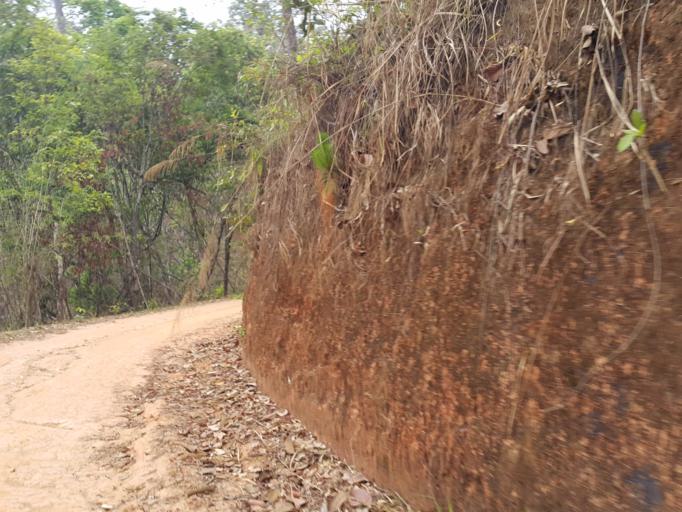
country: TH
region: Chiang Mai
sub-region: Amphoe Chiang Dao
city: Chiang Dao
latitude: 19.2874
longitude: 98.7577
